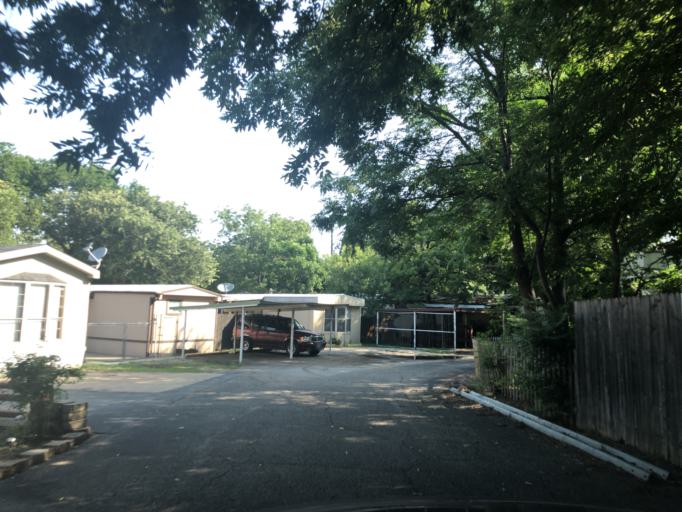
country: US
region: Texas
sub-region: Dallas County
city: Irving
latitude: 32.8058
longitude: -96.9910
